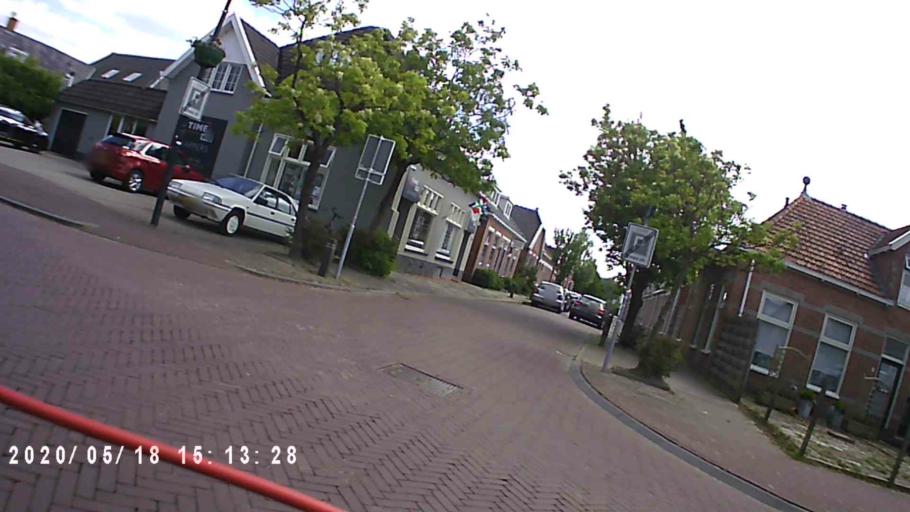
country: NL
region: Groningen
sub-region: Gemeente Winsum
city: Winsum
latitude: 53.3346
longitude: 6.5170
